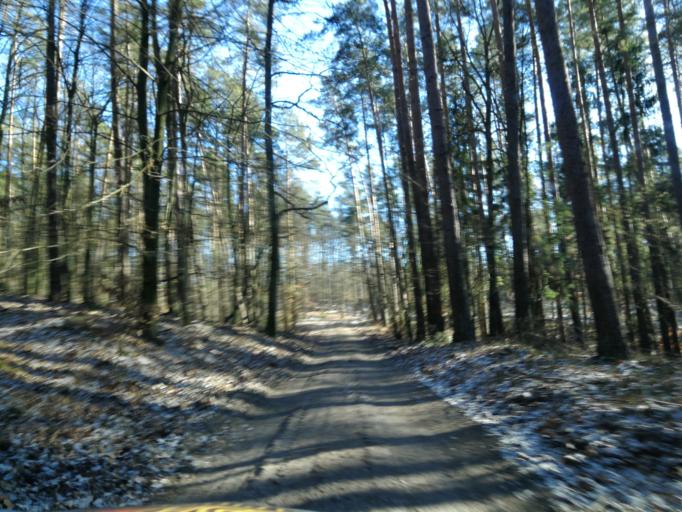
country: PL
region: Kujawsko-Pomorskie
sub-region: Powiat brodnicki
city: Gorzno
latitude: 53.2200
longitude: 19.7088
